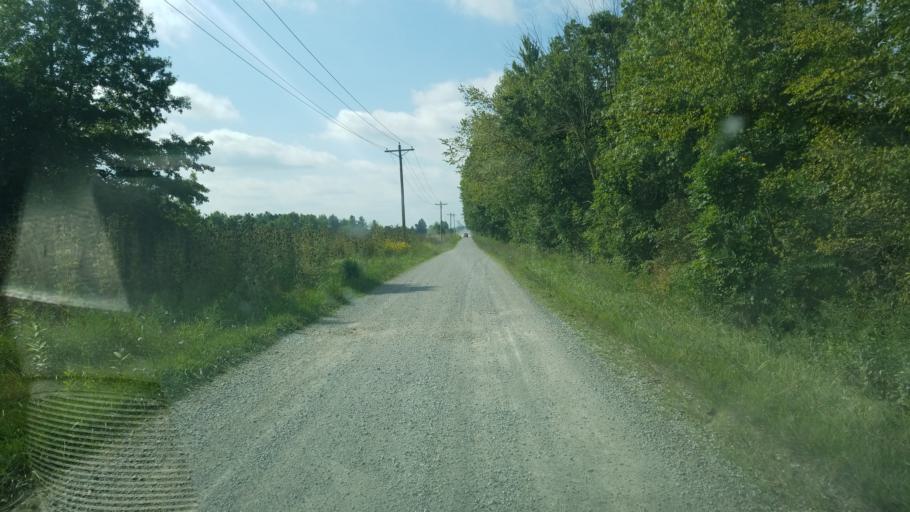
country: US
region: Ohio
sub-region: Wyandot County
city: Upper Sandusky
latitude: 40.7054
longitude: -83.3623
